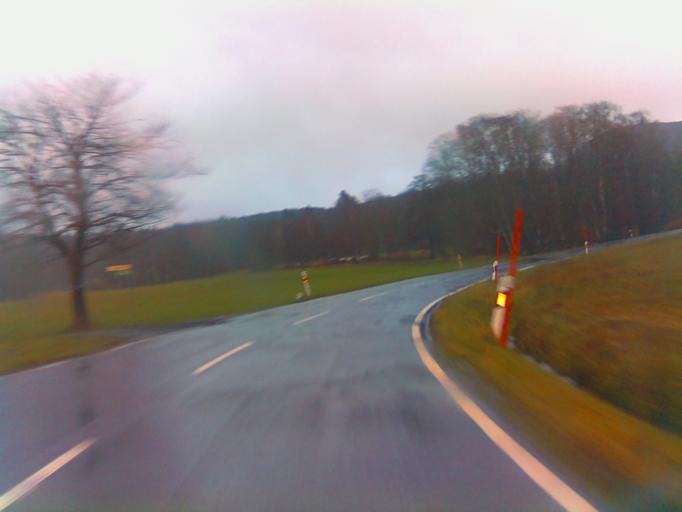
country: DE
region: Thuringia
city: Birx
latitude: 50.4951
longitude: 10.0120
